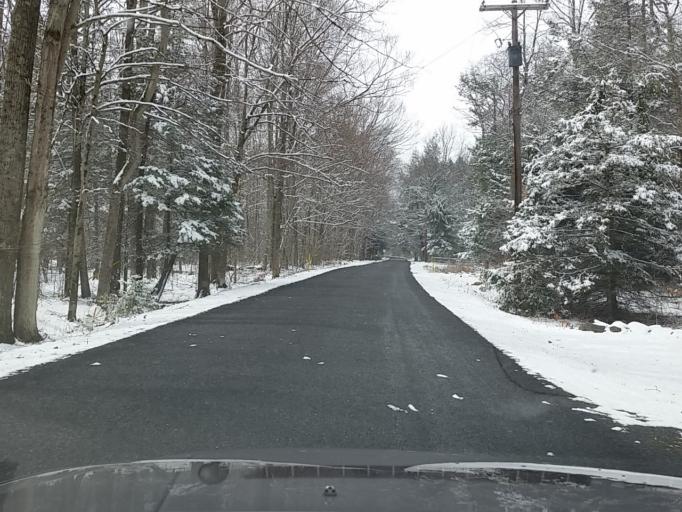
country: US
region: Pennsylvania
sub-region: Sullivan County
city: Laporte
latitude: 41.3056
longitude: -76.4226
